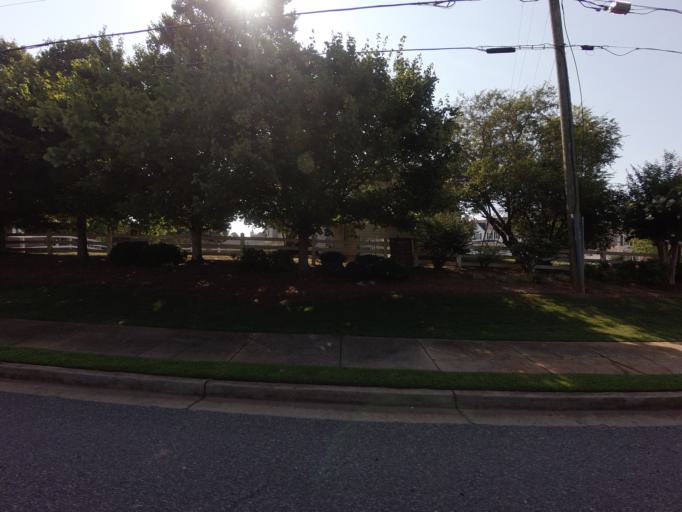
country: US
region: Georgia
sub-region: Fulton County
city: Johns Creek
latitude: 34.0822
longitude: -84.2053
